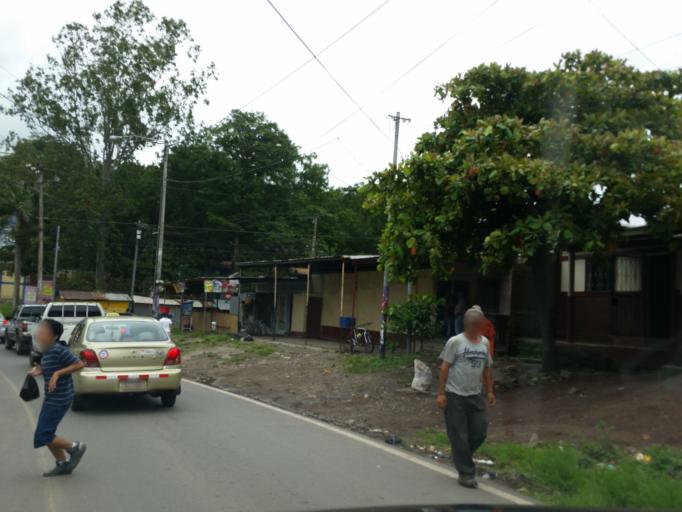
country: NI
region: Matagalpa
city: Matagalpa
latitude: 12.9286
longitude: -85.9217
